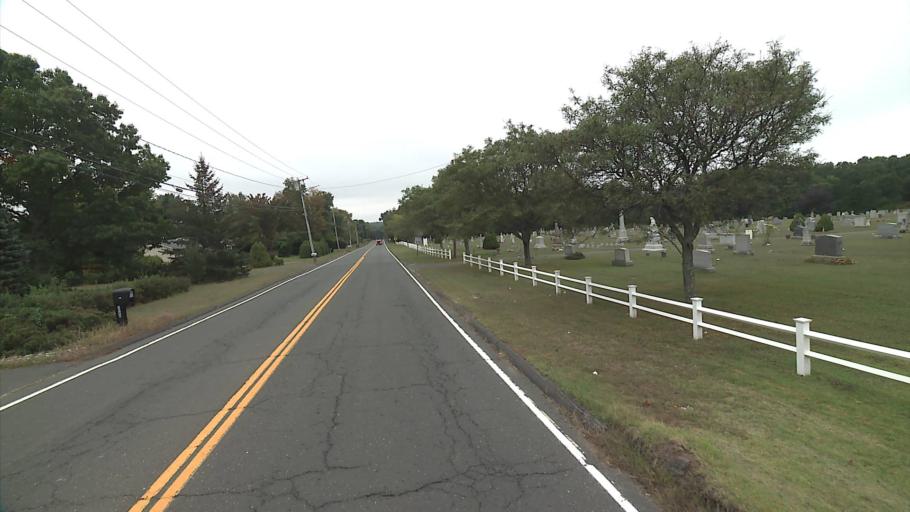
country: US
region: Connecticut
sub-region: Hartford County
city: Windsor Locks
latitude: 41.9138
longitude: -72.6758
